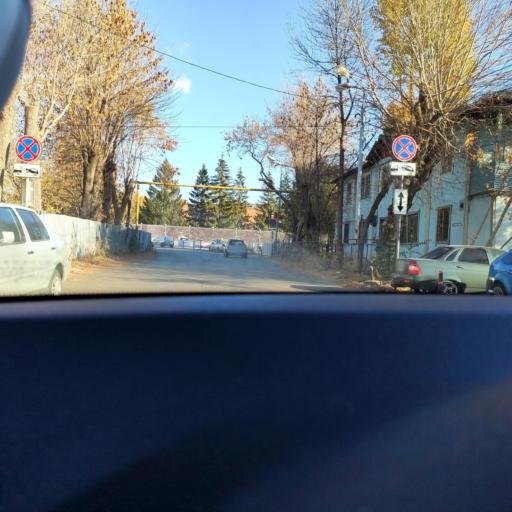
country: RU
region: Samara
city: Petra-Dubrava
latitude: 53.2415
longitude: 50.2788
